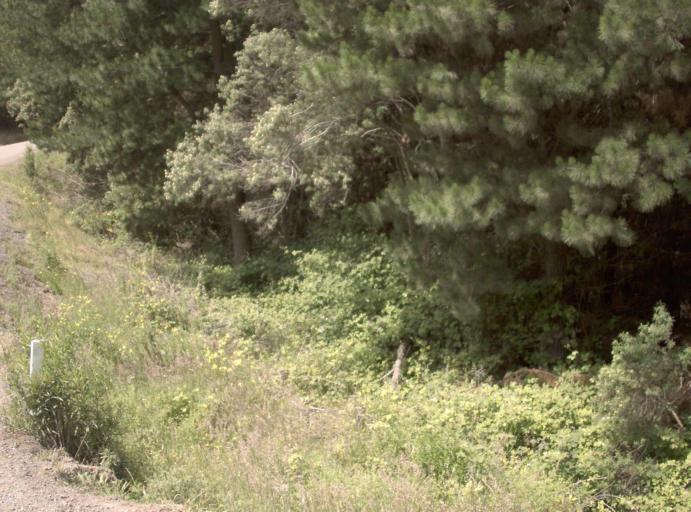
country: AU
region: Victoria
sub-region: Latrobe
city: Traralgon
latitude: -38.3877
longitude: 146.6615
